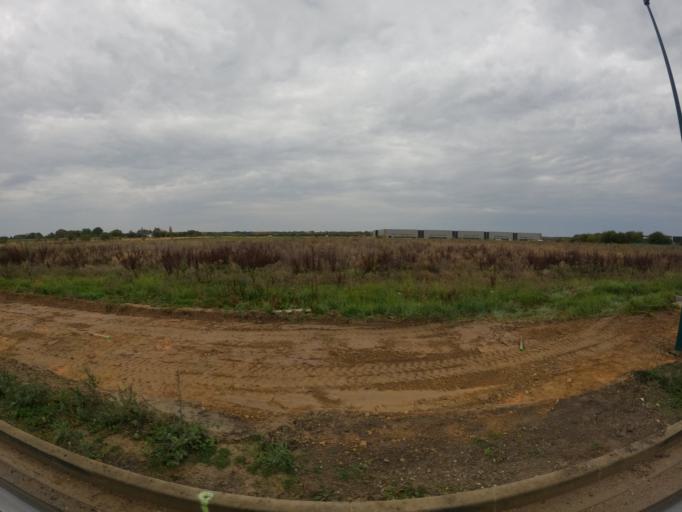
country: FR
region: Ile-de-France
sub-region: Departement de Seine-et-Marne
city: Serris
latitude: 48.8431
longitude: 2.8022
